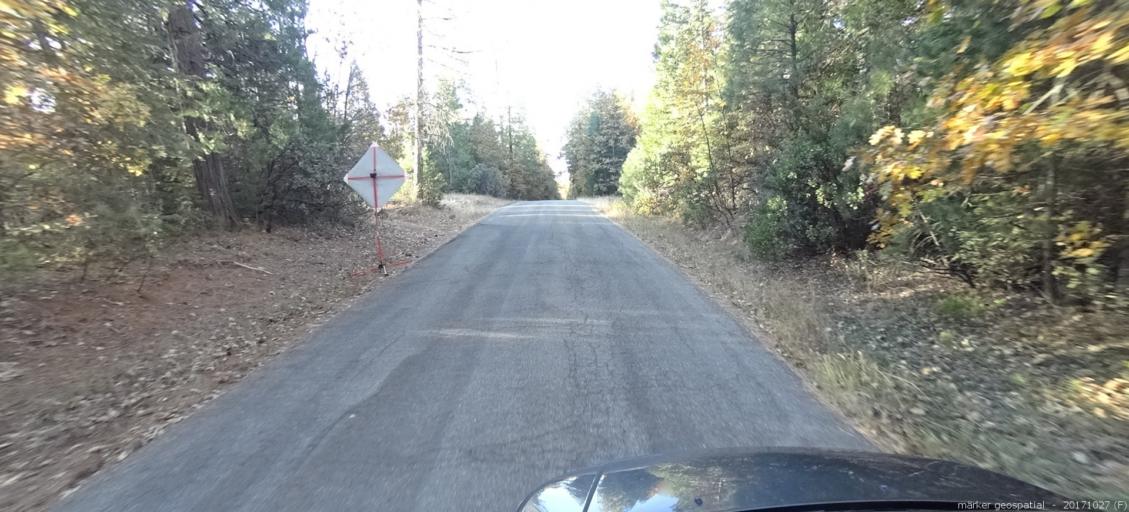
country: US
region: California
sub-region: Shasta County
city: Burney
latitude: 40.9294
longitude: -121.9490
